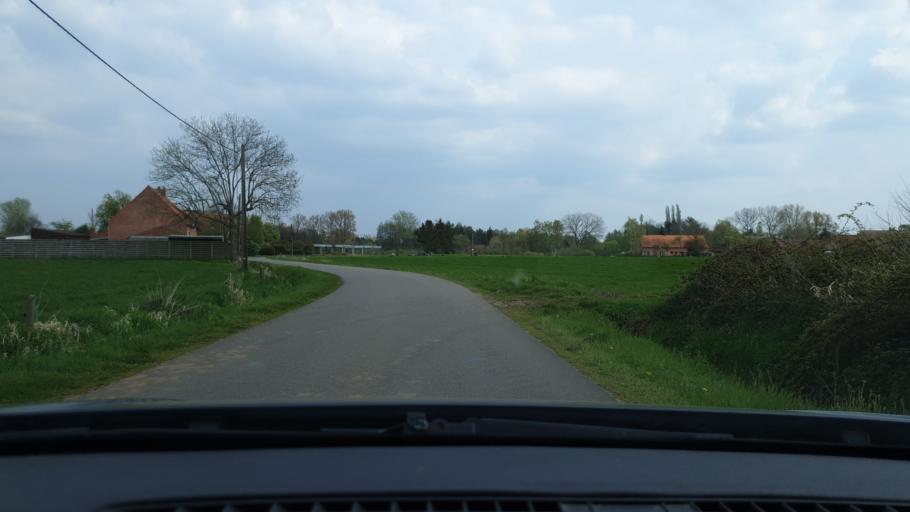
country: BE
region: Flanders
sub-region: Provincie Antwerpen
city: Geel
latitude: 51.1436
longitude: 4.9889
